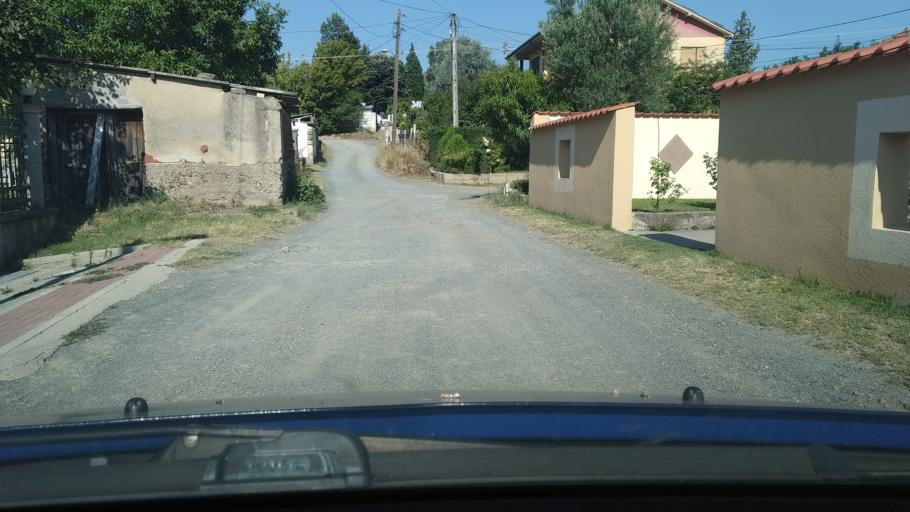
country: MK
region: Bogdanci
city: Bogdanci
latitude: 41.2052
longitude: 22.5828
